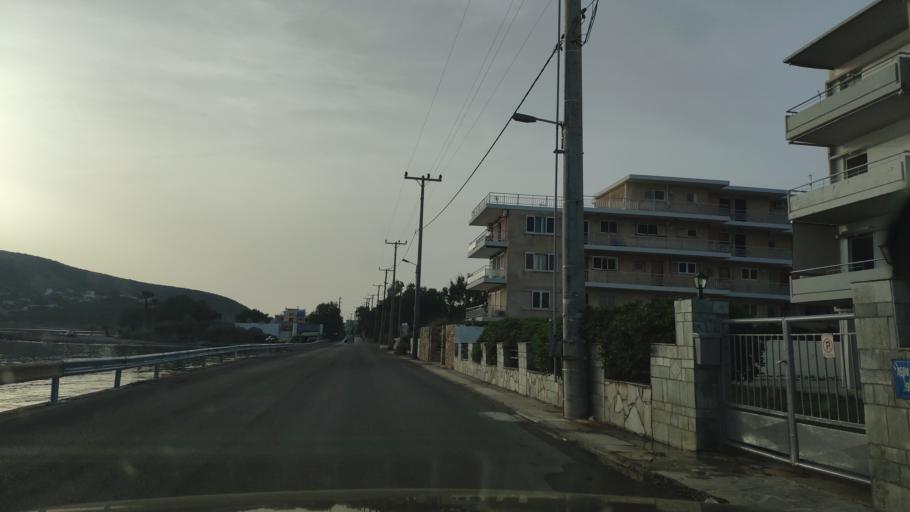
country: GR
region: Attica
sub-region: Nomarchia Anatolikis Attikis
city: Limin Mesoyaias
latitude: 37.8700
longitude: 24.0254
